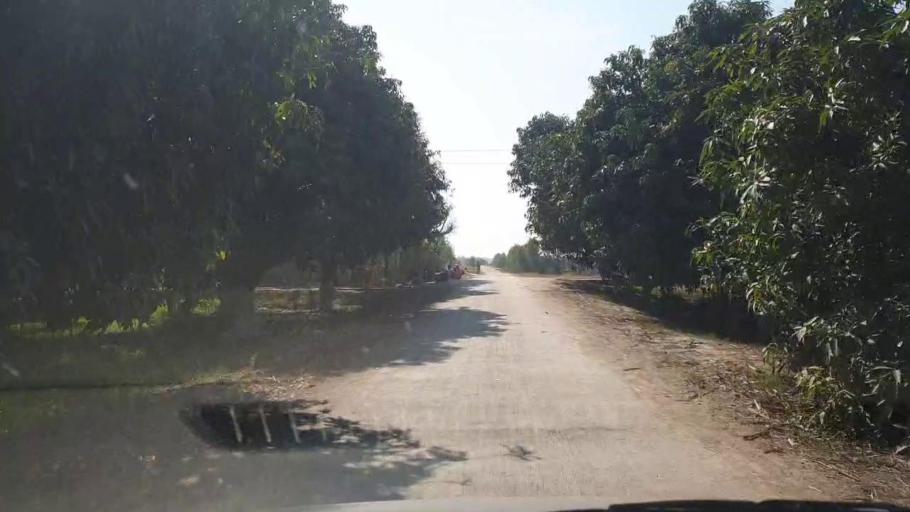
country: PK
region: Sindh
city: Tando Allahyar
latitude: 25.3996
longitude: 68.7817
